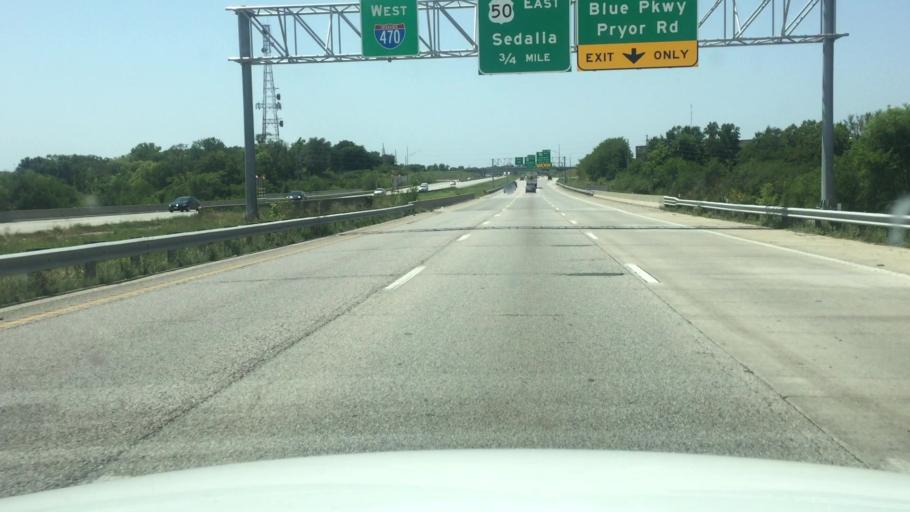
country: US
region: Missouri
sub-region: Jackson County
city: Lees Summit
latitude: 38.9395
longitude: -94.3949
